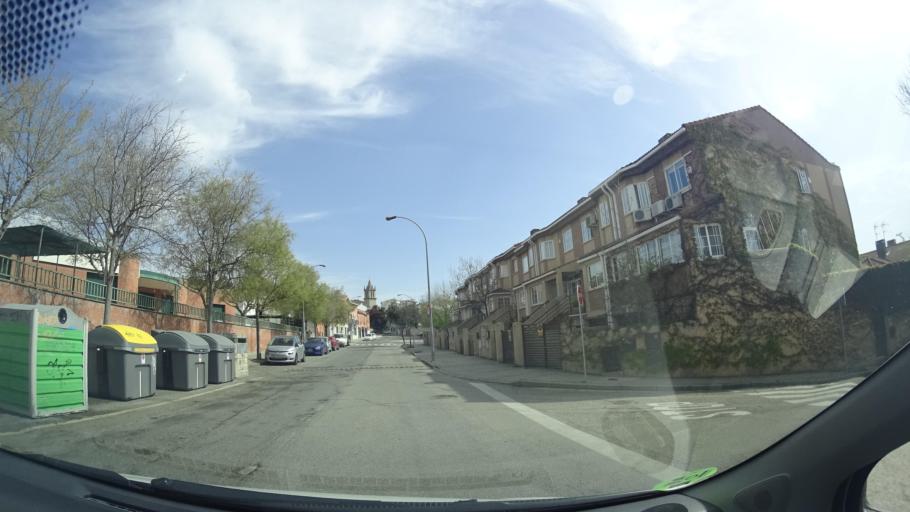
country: ES
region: Madrid
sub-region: Provincia de Madrid
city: Colmenar Viejo
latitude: 40.6545
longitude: -3.7700
